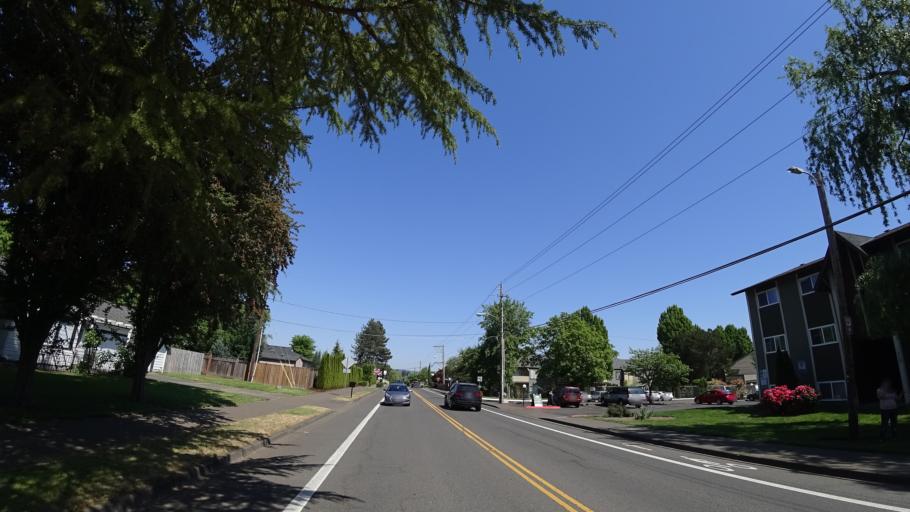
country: US
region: Oregon
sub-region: Washington County
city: Beaverton
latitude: 45.4937
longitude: -122.8042
